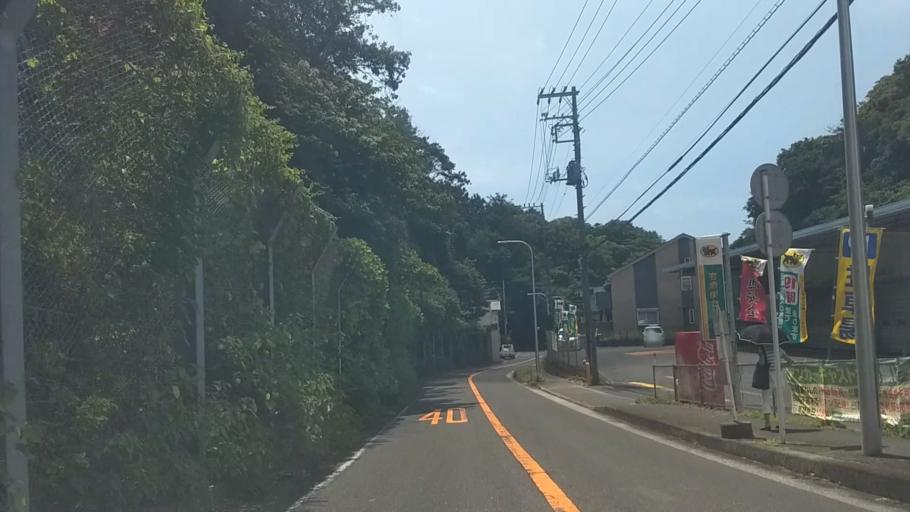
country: JP
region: Kanagawa
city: Kamakura
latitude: 35.3057
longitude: 139.5627
